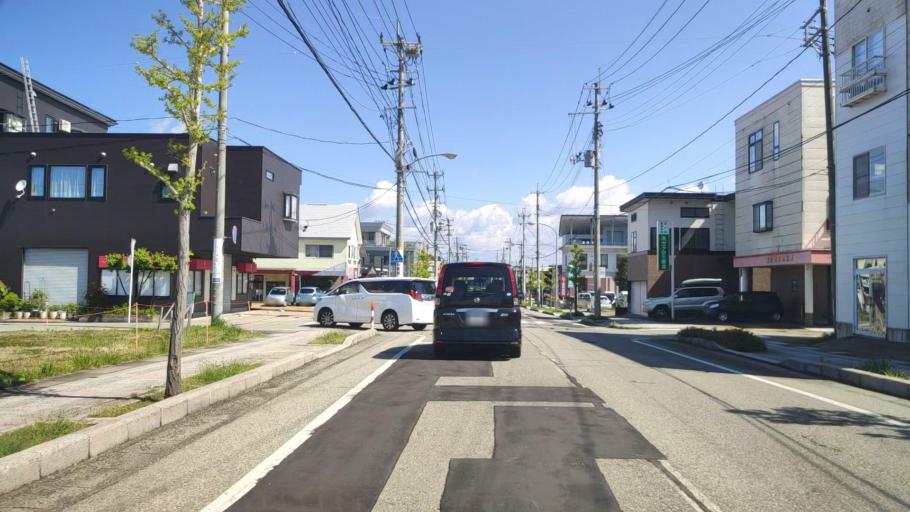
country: JP
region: Akita
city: Omagari
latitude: 39.4605
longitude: 140.4812
